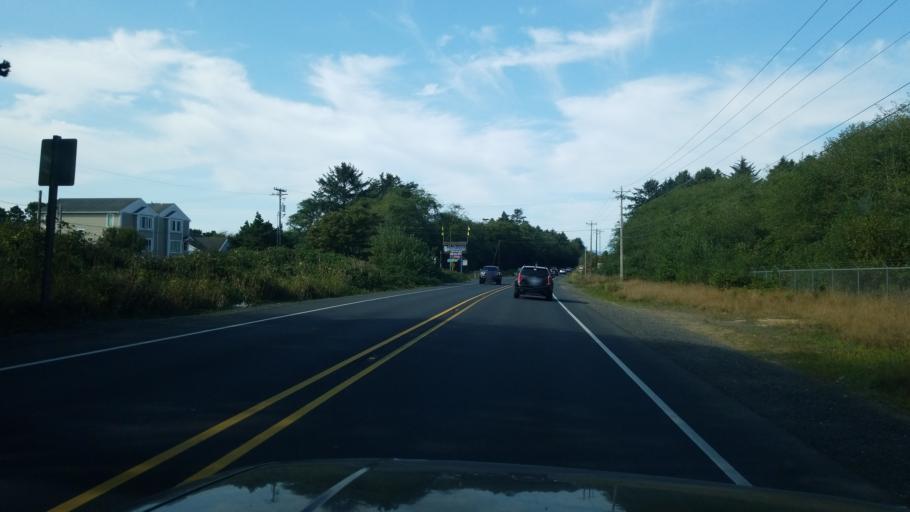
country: US
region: Oregon
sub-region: Tillamook County
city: Rockaway Beach
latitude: 45.5871
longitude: -123.9477
